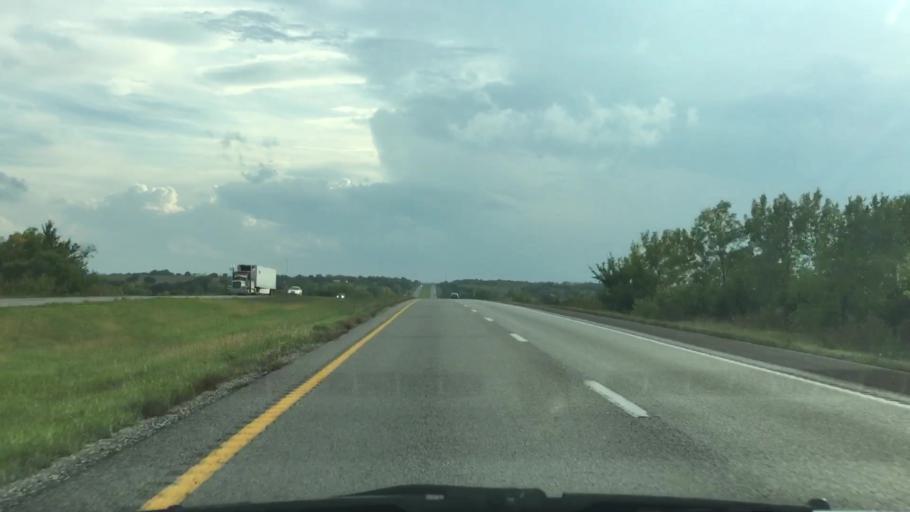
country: US
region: Missouri
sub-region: Daviess County
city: Gallatin
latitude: 39.9208
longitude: -94.1403
